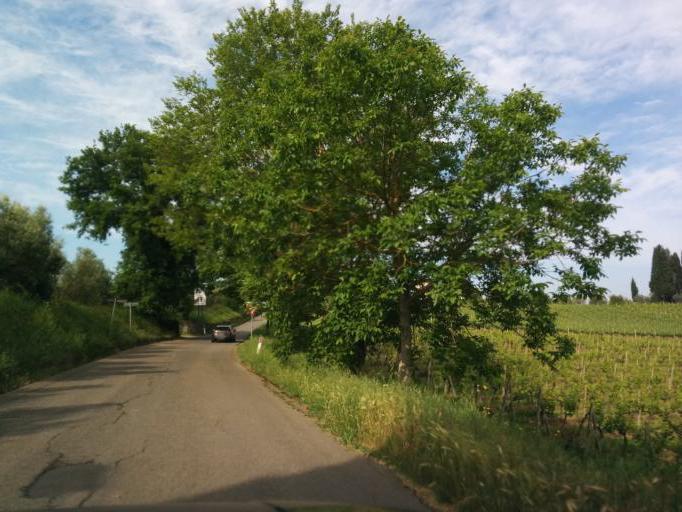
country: IT
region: Tuscany
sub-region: Province of Florence
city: San Casciano in Val di Pesa
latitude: 43.6818
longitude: 11.1959
